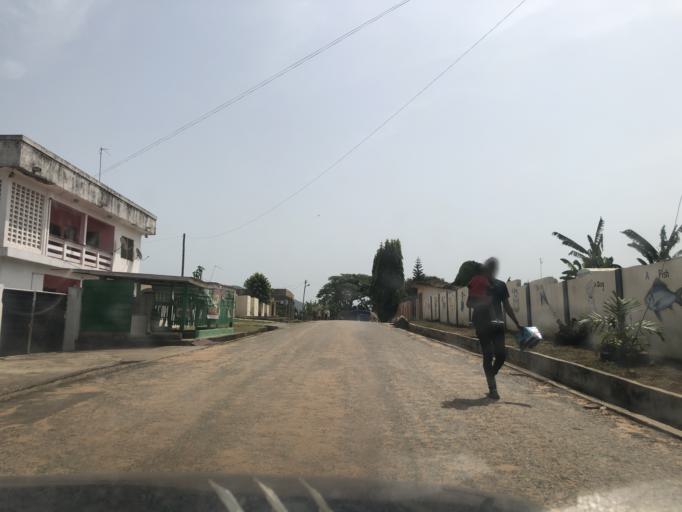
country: GH
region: Eastern
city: Koforidua
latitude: 6.0923
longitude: -0.2729
